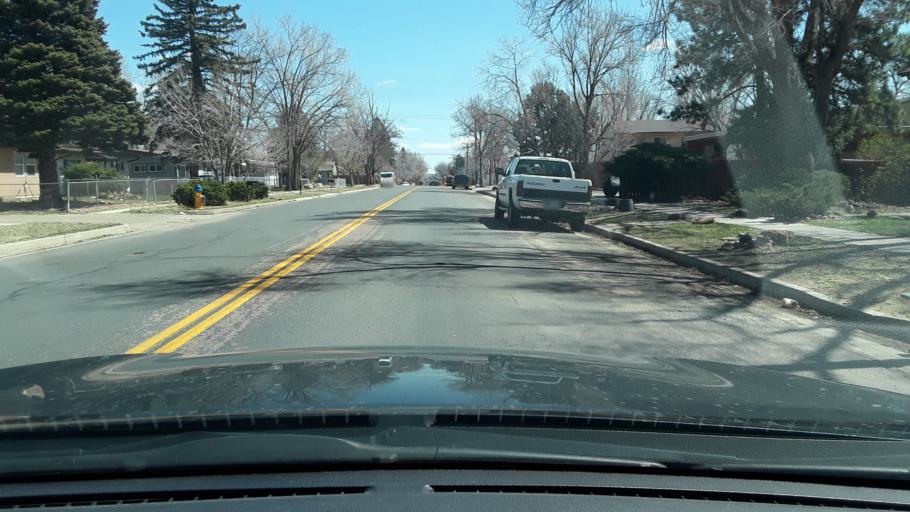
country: US
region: Colorado
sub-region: El Paso County
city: Colorado Springs
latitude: 38.8489
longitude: -104.7820
